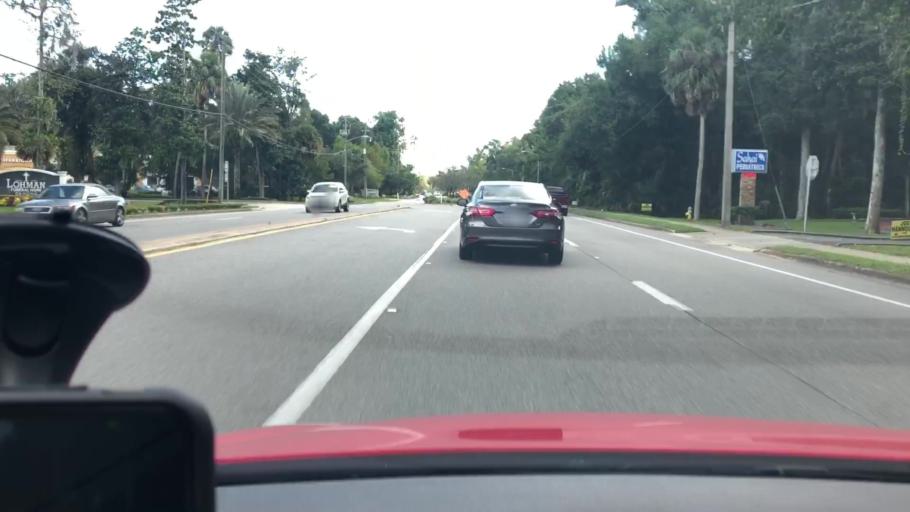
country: US
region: Florida
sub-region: Volusia County
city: Ormond Beach
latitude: 29.2789
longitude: -81.0778
